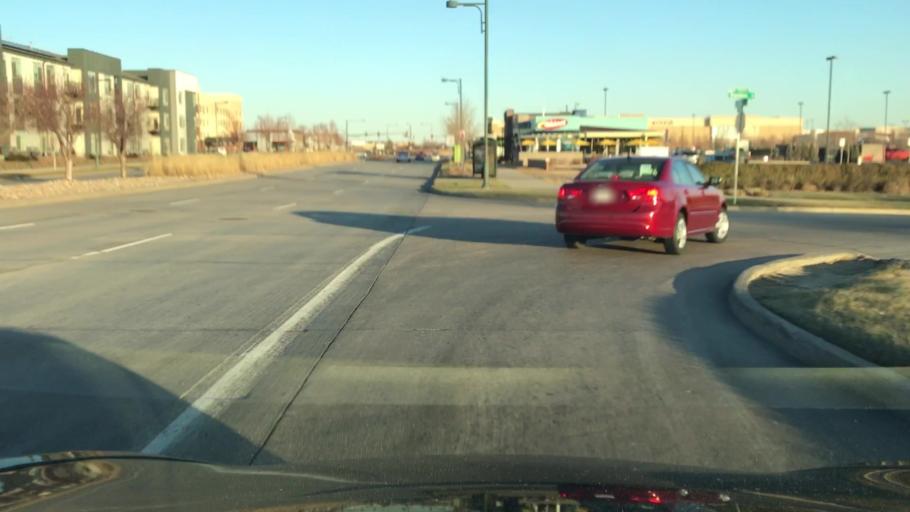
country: US
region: Colorado
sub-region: Adams County
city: Commerce City
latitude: 39.7855
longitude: -104.8965
